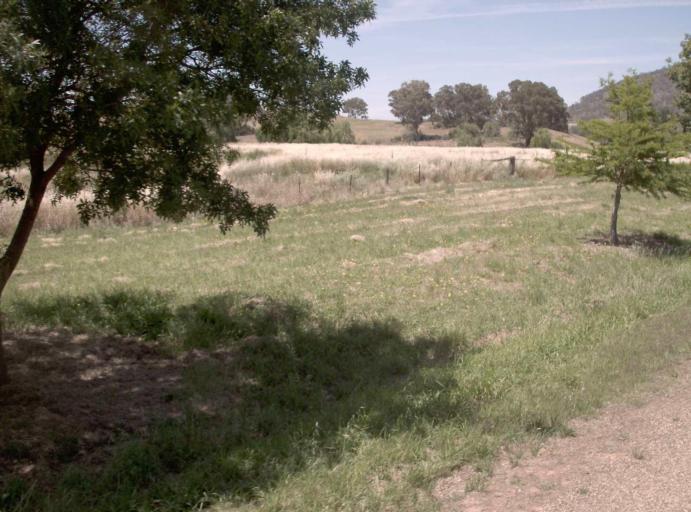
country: AU
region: Victoria
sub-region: East Gippsland
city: Bairnsdale
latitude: -37.2515
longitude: 147.7119
